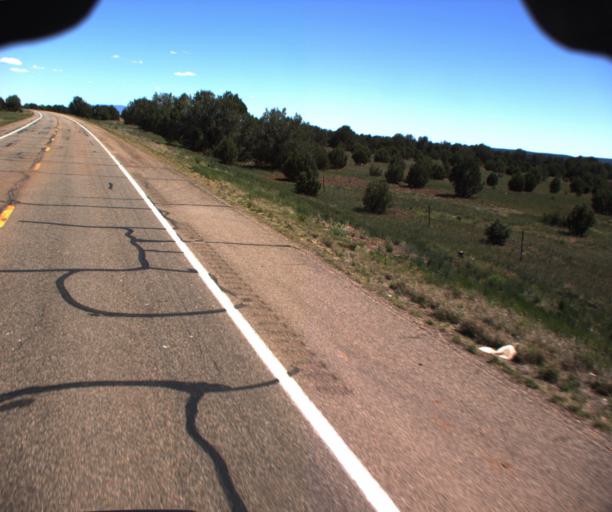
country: US
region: Arizona
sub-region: Yavapai County
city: Paulden
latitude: 35.0979
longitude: -112.4224
